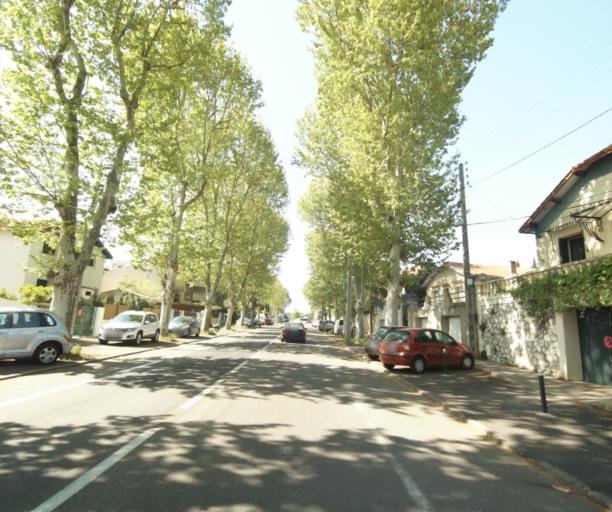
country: FR
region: Languedoc-Roussillon
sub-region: Departement de l'Herault
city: Montpellier
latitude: 43.6158
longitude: 3.8561
